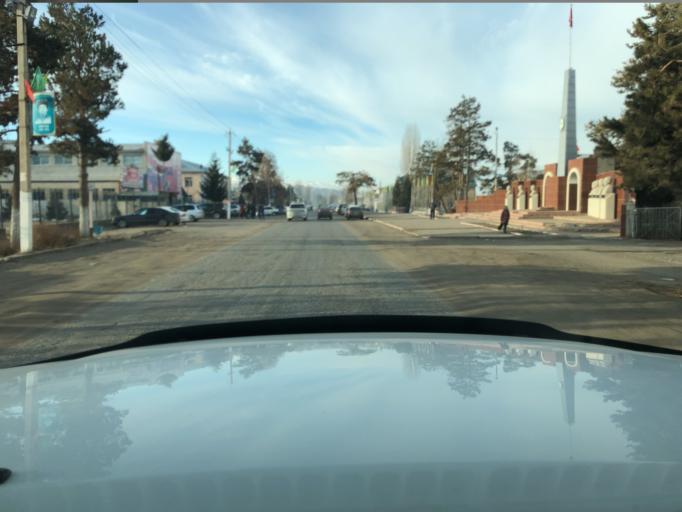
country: KG
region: Ysyk-Koel
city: Pokrovka
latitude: 42.3415
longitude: 78.0032
